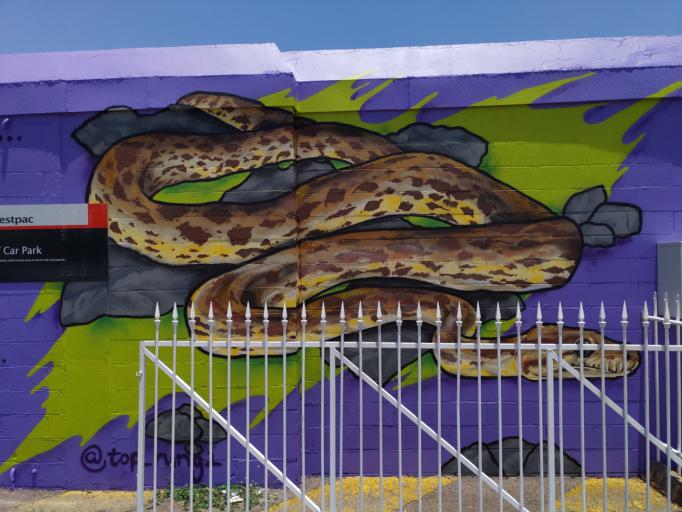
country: AU
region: Northern Territory
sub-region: Darwin
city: Darwin
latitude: -12.4640
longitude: 130.8438
